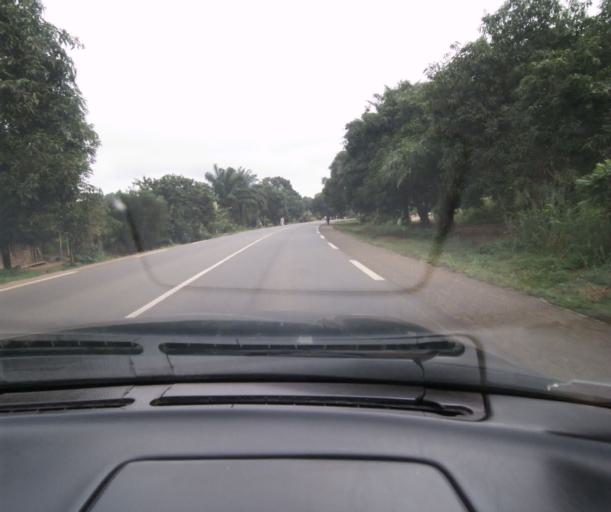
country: CM
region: Centre
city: Saa
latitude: 4.3380
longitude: 11.2834
